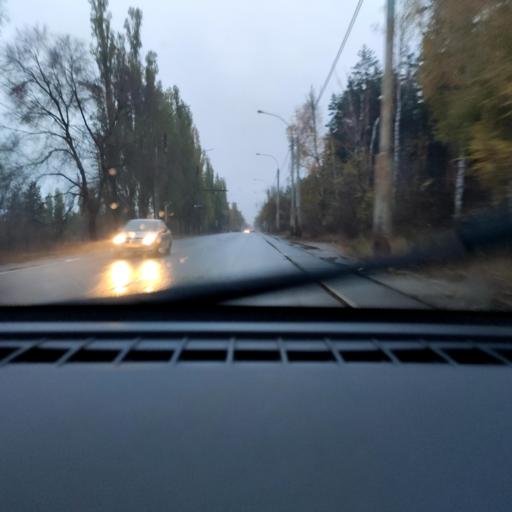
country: RU
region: Voronezj
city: Somovo
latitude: 51.7077
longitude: 39.2917
